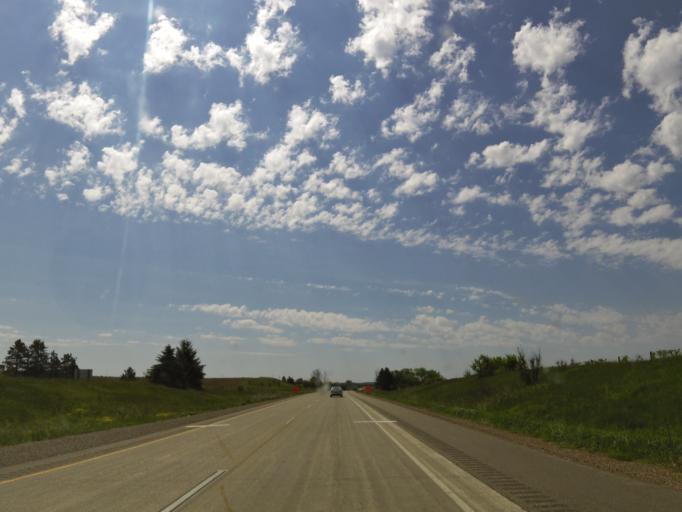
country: US
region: Wisconsin
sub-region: Eau Claire County
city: Fall Creek
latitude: 44.6663
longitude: -91.3179
